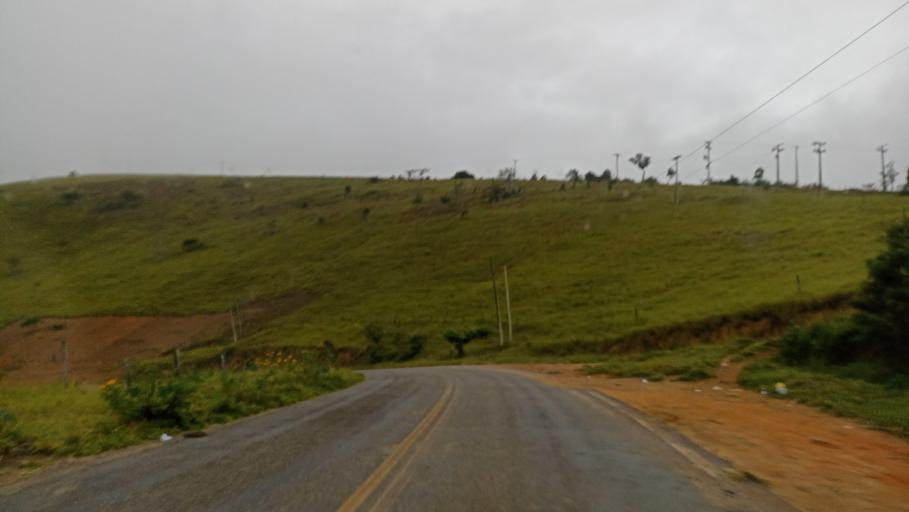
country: BR
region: Bahia
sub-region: Itanhem
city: Itanhem
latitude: -16.7328
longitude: -40.4360
